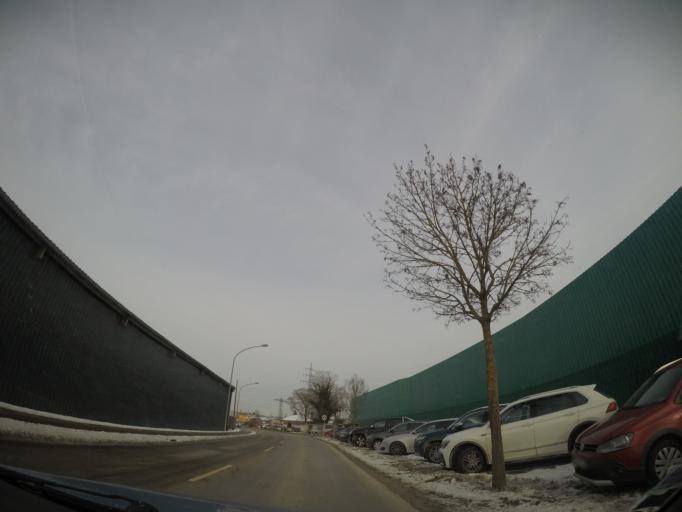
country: DE
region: Bavaria
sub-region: Swabia
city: Neu-Ulm
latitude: 48.3971
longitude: 10.0304
